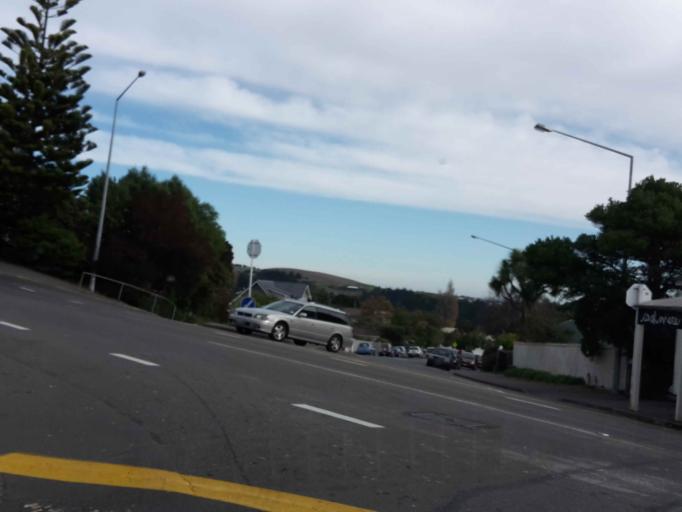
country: NZ
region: Canterbury
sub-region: Christchurch City
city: Christchurch
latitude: -43.5770
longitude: 172.6305
